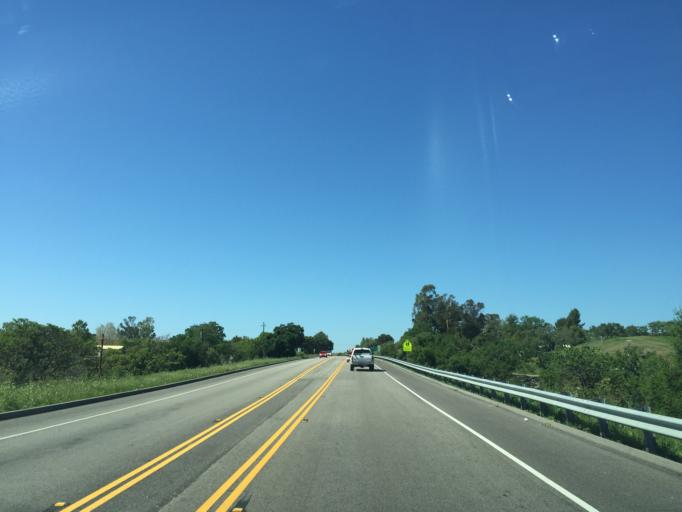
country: US
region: California
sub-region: Santa Barbara County
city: Los Olivos
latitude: 34.6639
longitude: -120.1080
